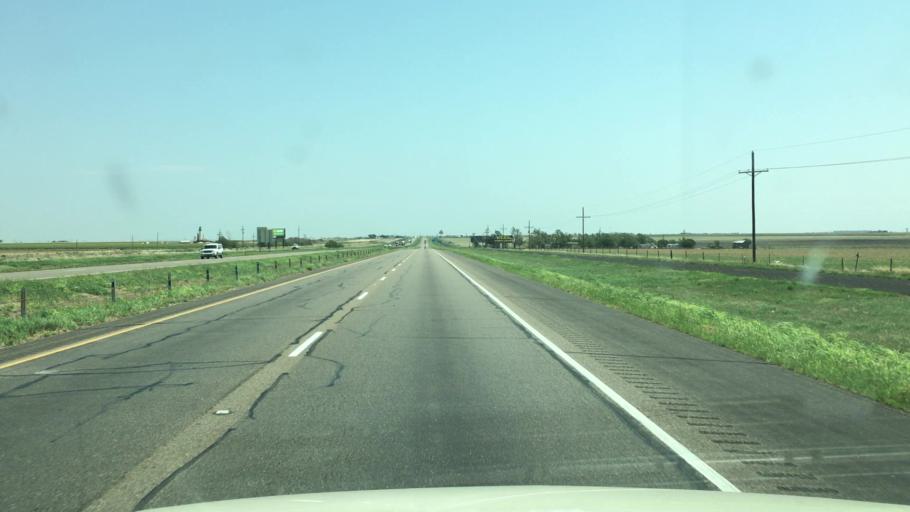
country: US
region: Texas
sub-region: Potter County
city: Bushland
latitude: 35.1907
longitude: -102.0427
